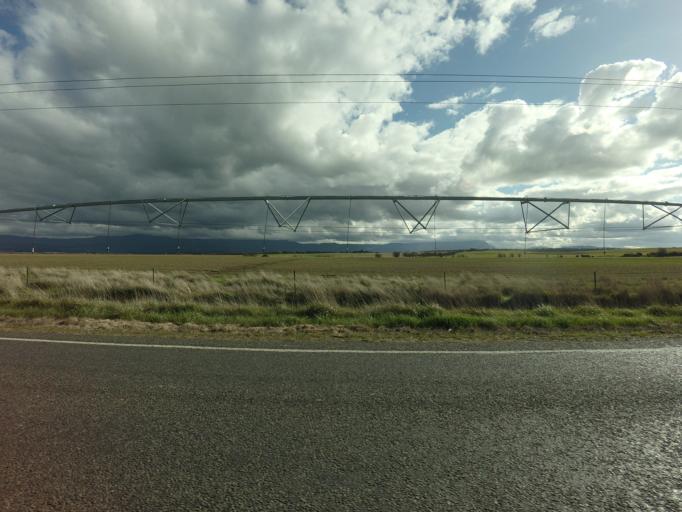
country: AU
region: Tasmania
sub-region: Northern Midlands
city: Longford
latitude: -41.7059
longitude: 147.0787
